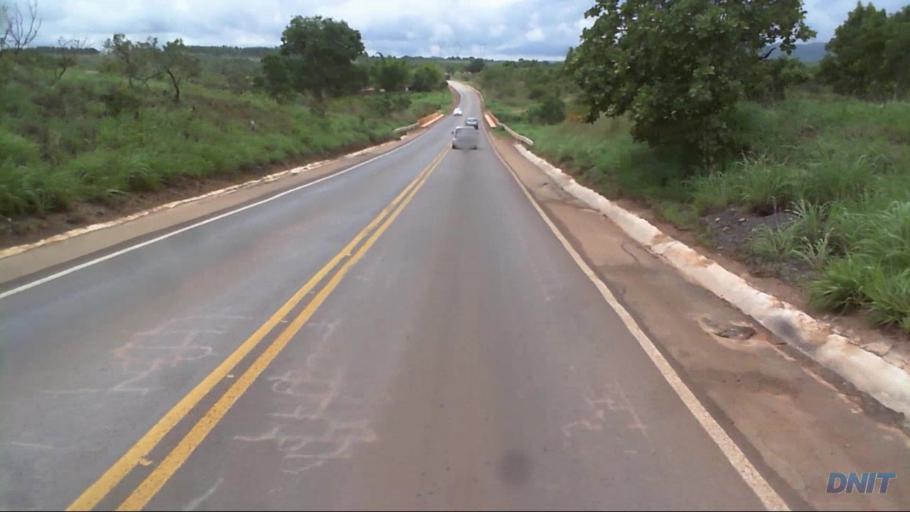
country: BR
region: Goias
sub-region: Padre Bernardo
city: Padre Bernardo
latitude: -15.3700
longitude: -48.2194
